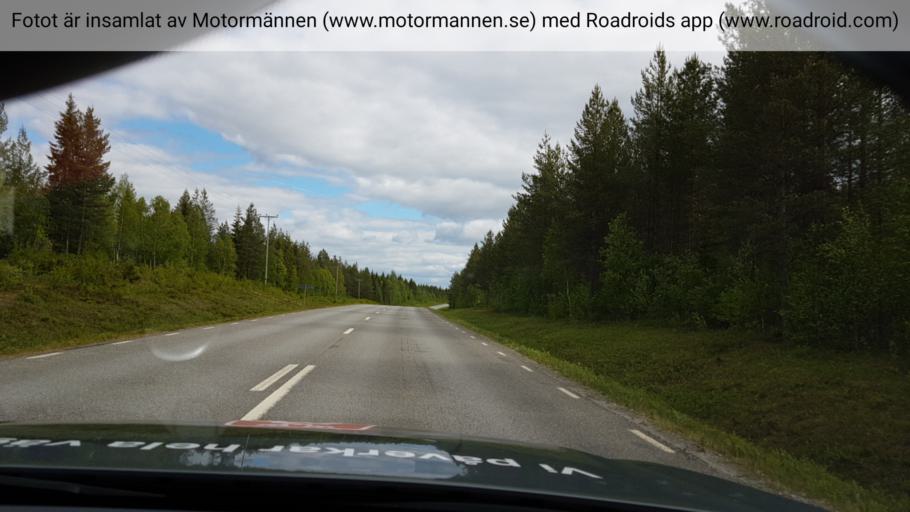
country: SE
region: Jaemtland
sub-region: Stroemsunds Kommun
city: Stroemsund
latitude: 64.2786
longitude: 15.3689
